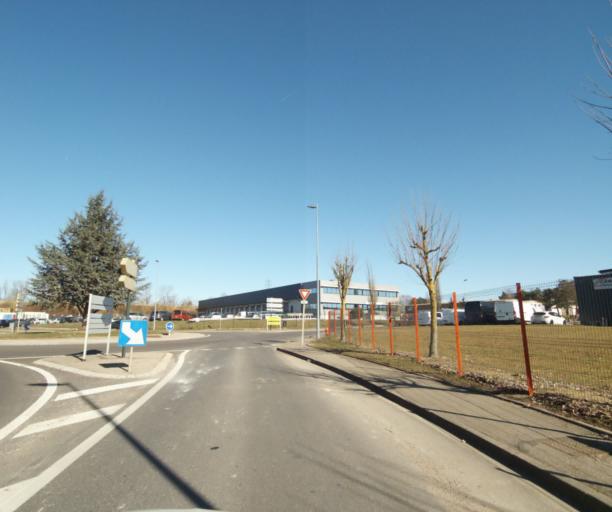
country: FR
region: Lorraine
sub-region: Departement de Meurthe-et-Moselle
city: Fleville-devant-Nancy
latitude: 48.6166
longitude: 6.2040
